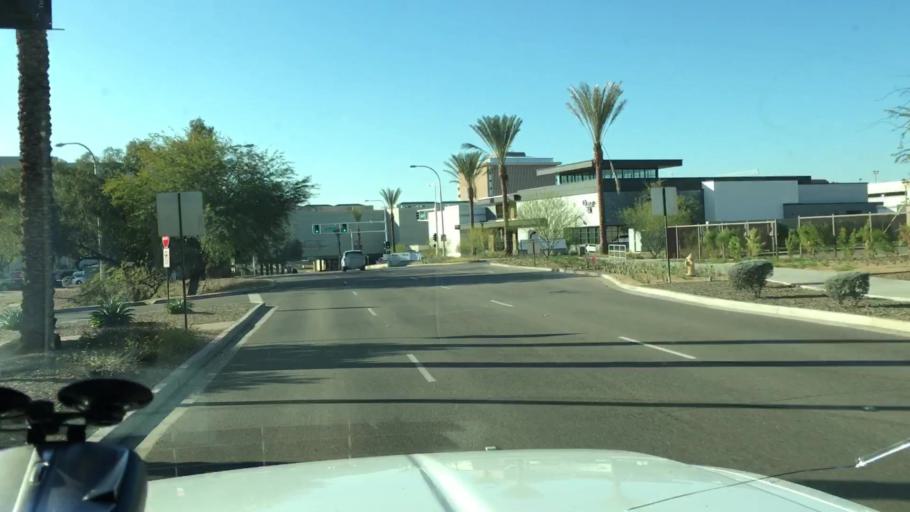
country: US
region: Arizona
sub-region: Maricopa County
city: Paradise Valley
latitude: 33.5061
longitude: -111.9301
